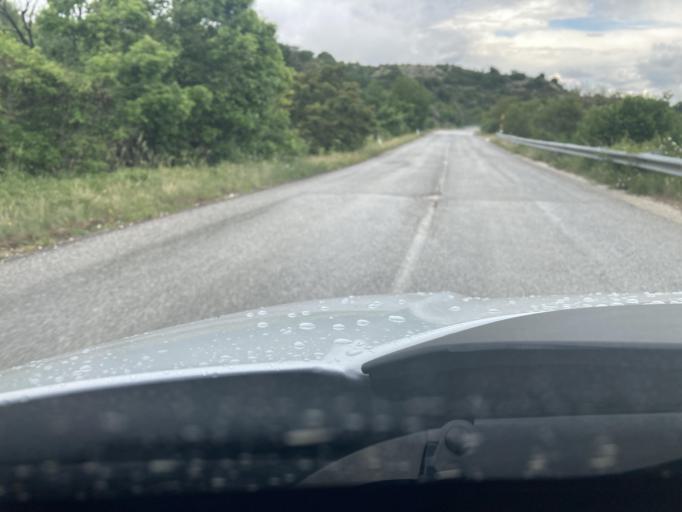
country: IT
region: Abruzzo
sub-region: Provincia dell' Aquila
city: Villa Sant'Angelo
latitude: 42.2425
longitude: 13.5251
